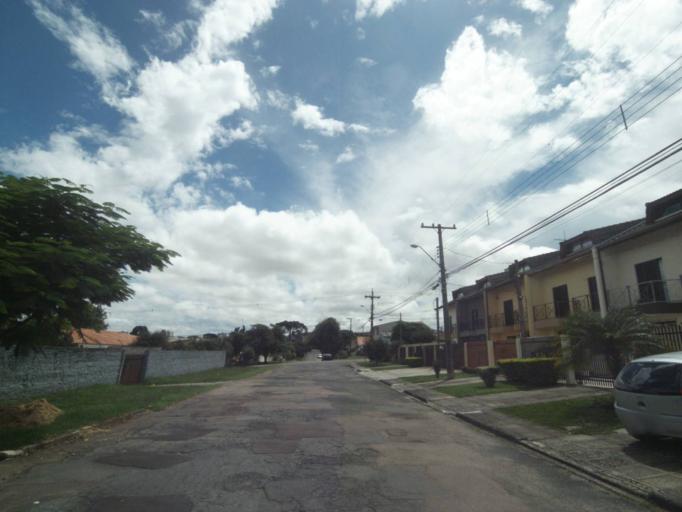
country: BR
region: Parana
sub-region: Curitiba
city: Curitiba
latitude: -25.4839
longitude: -49.2797
